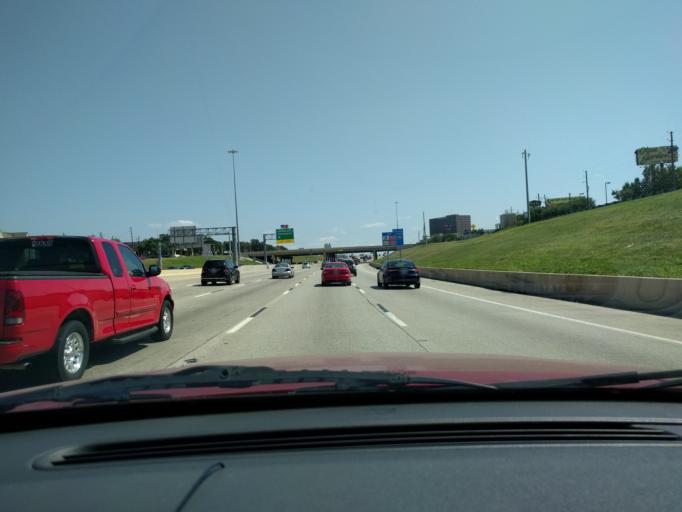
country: US
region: Texas
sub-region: Dallas County
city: Richardson
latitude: 32.9180
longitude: -96.7458
